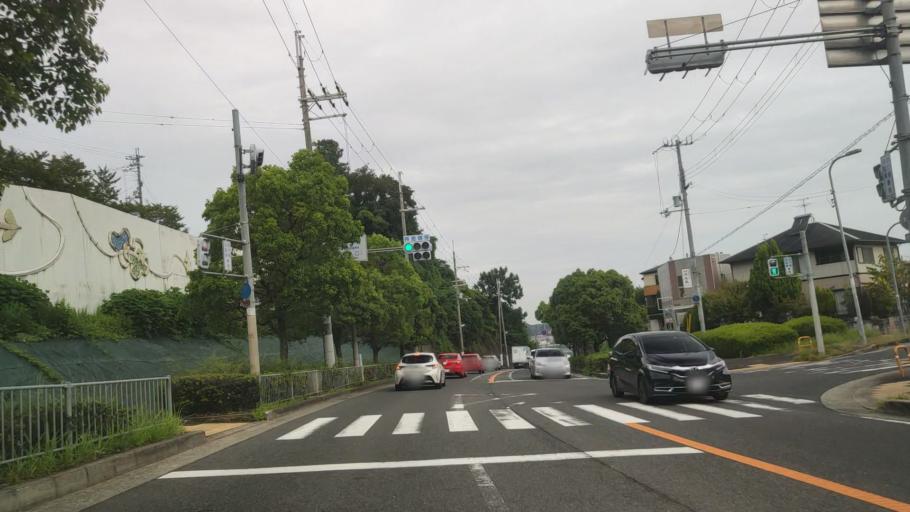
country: JP
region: Osaka
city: Tondabayashicho
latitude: 34.4355
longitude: 135.5581
